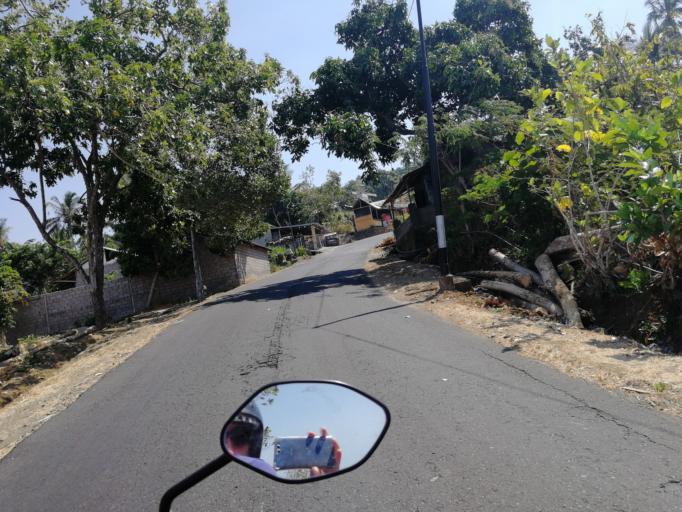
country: ID
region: Bali
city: Banjar Kedisan
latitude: -8.1416
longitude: 115.3159
